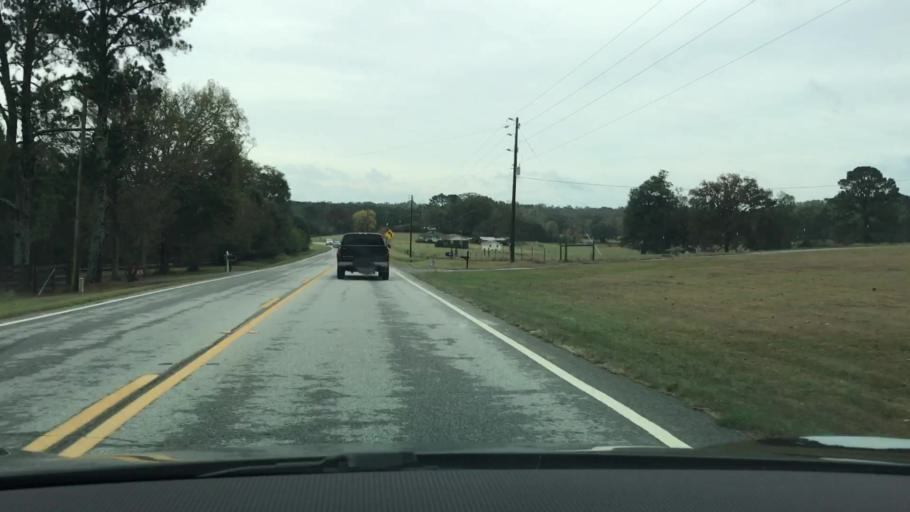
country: US
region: Georgia
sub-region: Greene County
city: Greensboro
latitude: 33.6484
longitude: -83.2342
